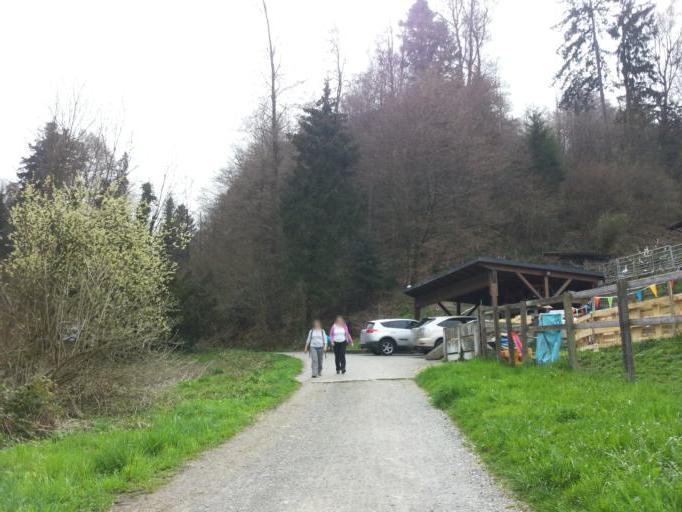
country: CH
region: Lucerne
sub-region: Lucerne-Land District
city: Meierskappel
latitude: 47.1137
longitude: 8.4745
